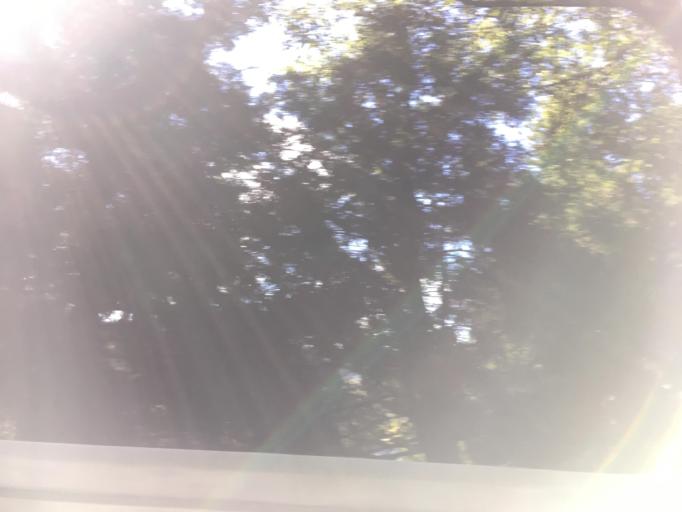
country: TW
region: Taiwan
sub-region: Yilan
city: Yilan
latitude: 24.5133
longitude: 121.5700
